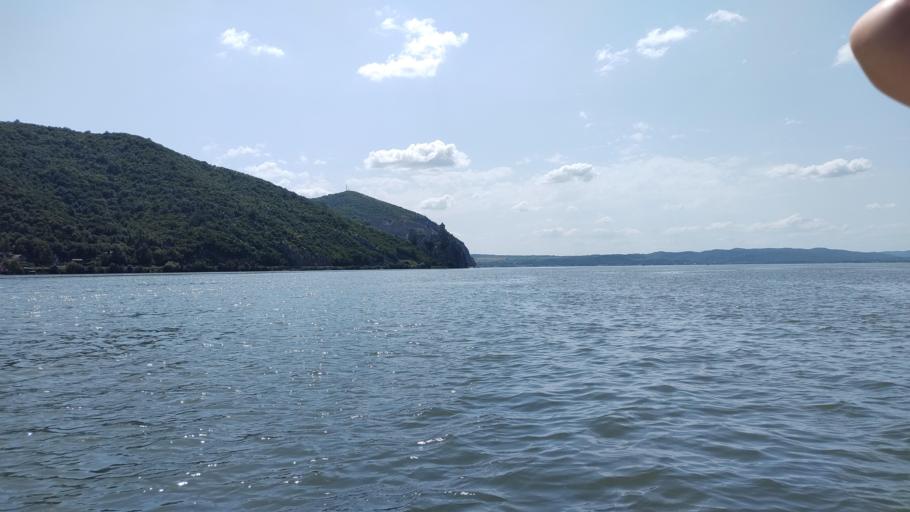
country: RO
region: Caras-Severin
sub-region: Comuna Pescari
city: Coronini
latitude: 44.6645
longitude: 21.6917
